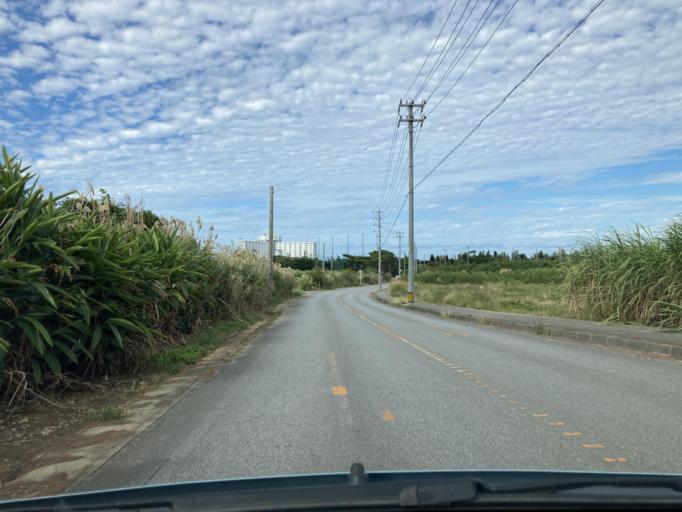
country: JP
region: Okinawa
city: Ishikawa
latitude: 26.4330
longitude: 127.7262
